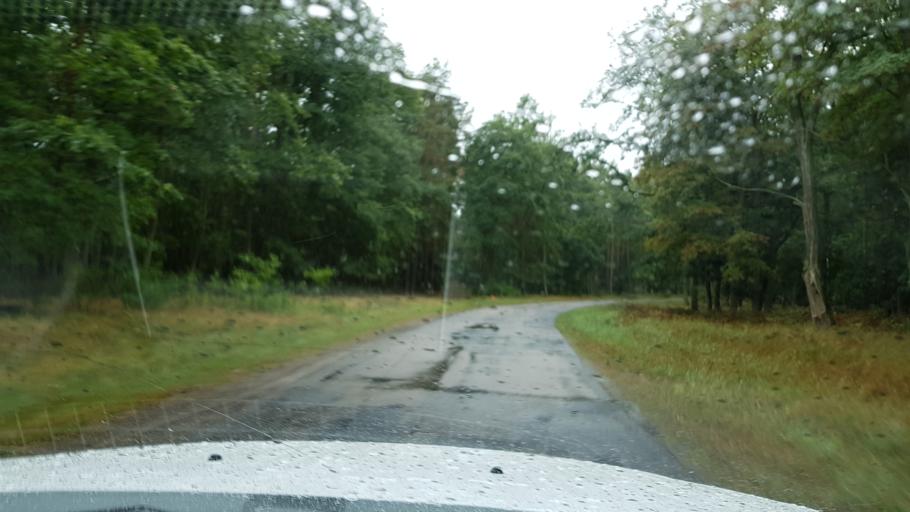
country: DE
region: Brandenburg
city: Schoneberg
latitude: 52.9527
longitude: 14.1843
